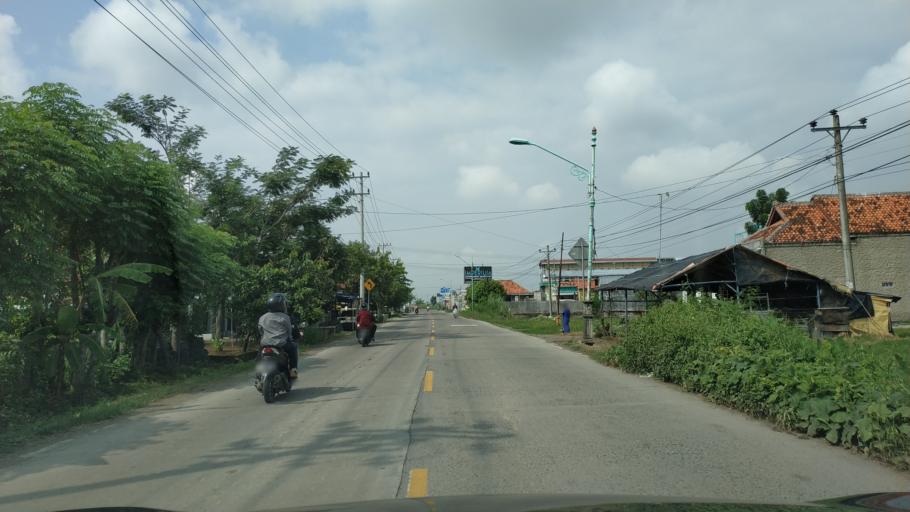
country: ID
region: Central Java
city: Ketanggungan
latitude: -6.9079
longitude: 108.8892
